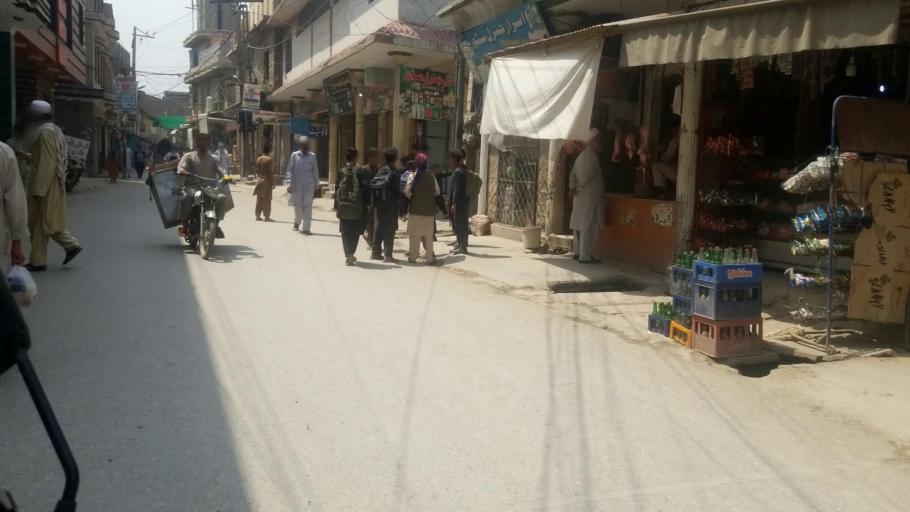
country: PK
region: Khyber Pakhtunkhwa
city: Peshawar
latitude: 34.0313
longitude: 71.5858
